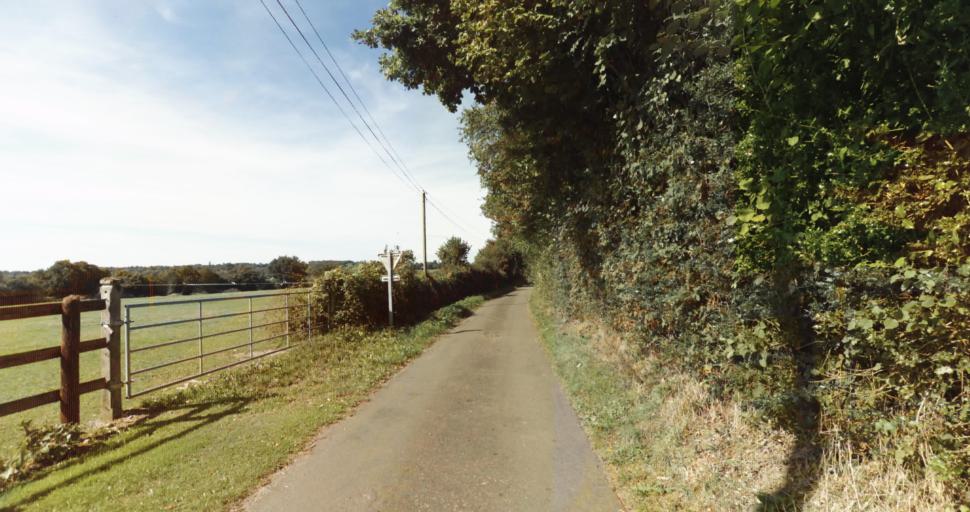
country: FR
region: Lower Normandy
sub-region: Departement de l'Orne
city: Gace
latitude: 48.7402
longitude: 0.2383
